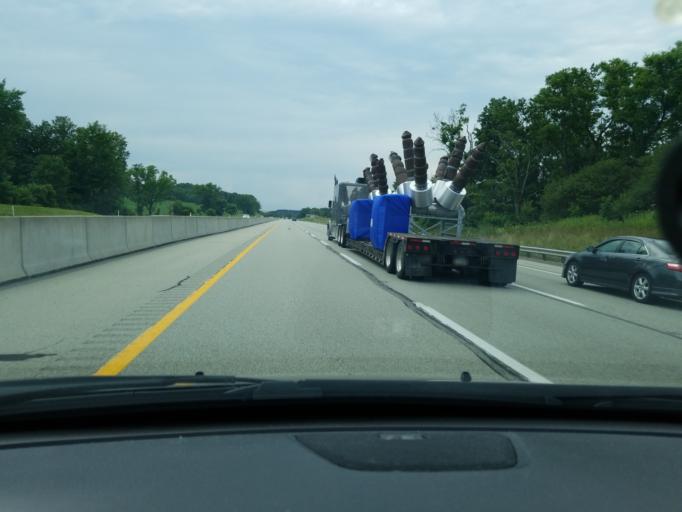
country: US
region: Pennsylvania
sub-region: Lawrence County
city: New Beaver
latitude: 40.8808
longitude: -80.4224
